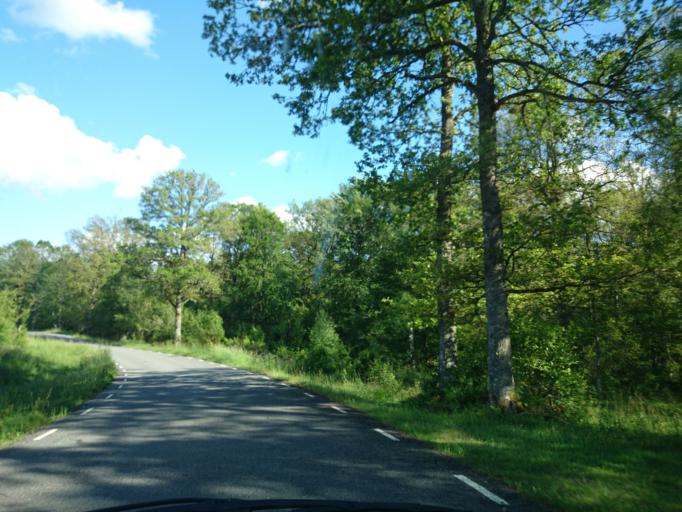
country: SE
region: Kronoberg
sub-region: Ljungby Kommun
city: Lagan
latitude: 57.0087
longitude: 13.9269
